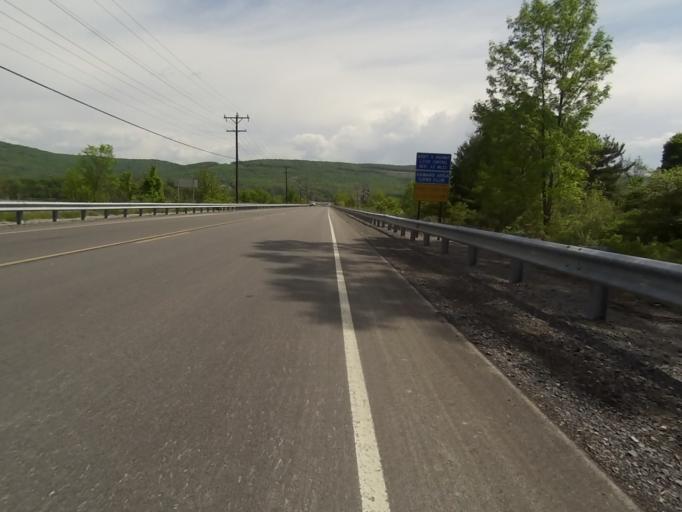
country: US
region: Pennsylvania
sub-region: Centre County
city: Zion
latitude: 41.0217
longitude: -77.6696
